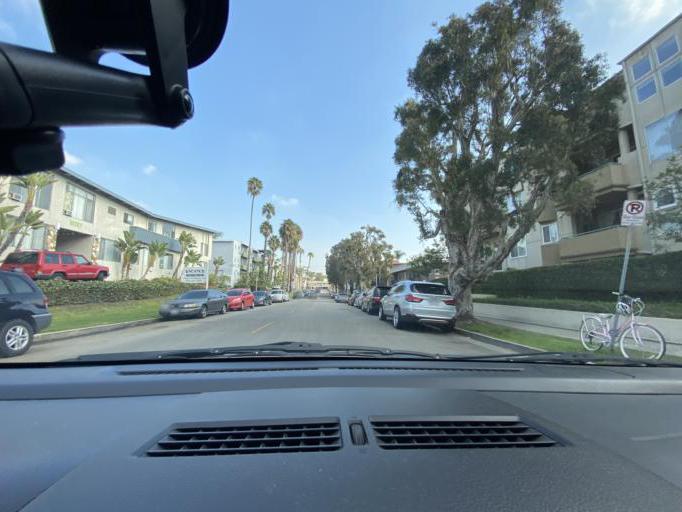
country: US
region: California
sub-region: Los Angeles County
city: Culver City
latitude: 34.0258
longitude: -118.4153
